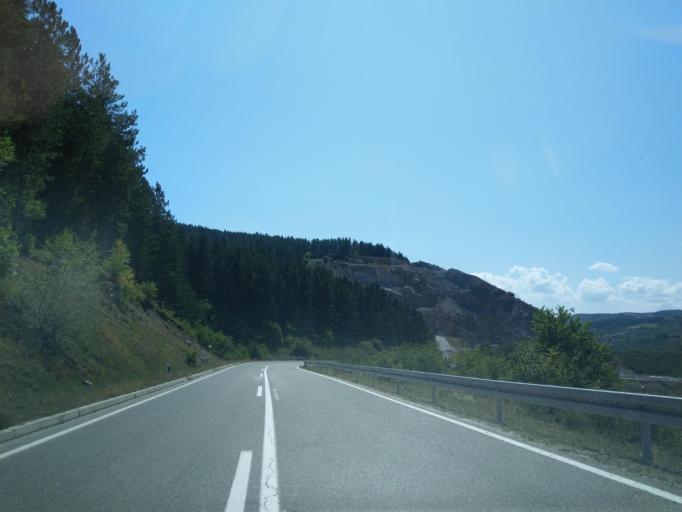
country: RS
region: Central Serbia
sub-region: Zlatiborski Okrug
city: Sjenica
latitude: 43.3000
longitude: 19.9352
